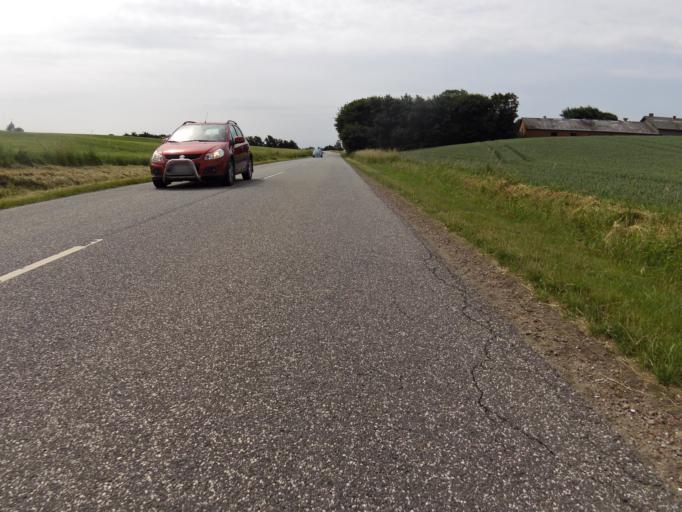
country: DK
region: Central Jutland
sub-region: Struer Kommune
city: Struer
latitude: 56.4353
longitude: 8.6288
